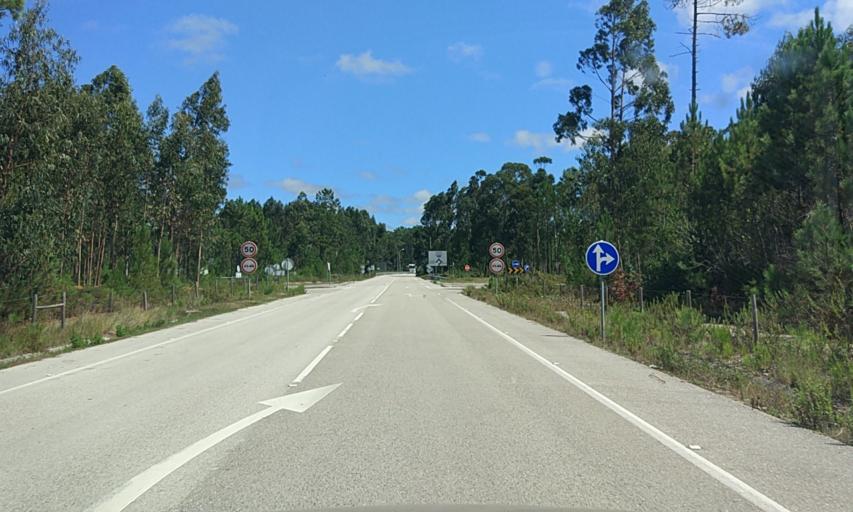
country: PT
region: Coimbra
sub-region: Mira
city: Mira
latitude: 40.3373
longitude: -8.7362
